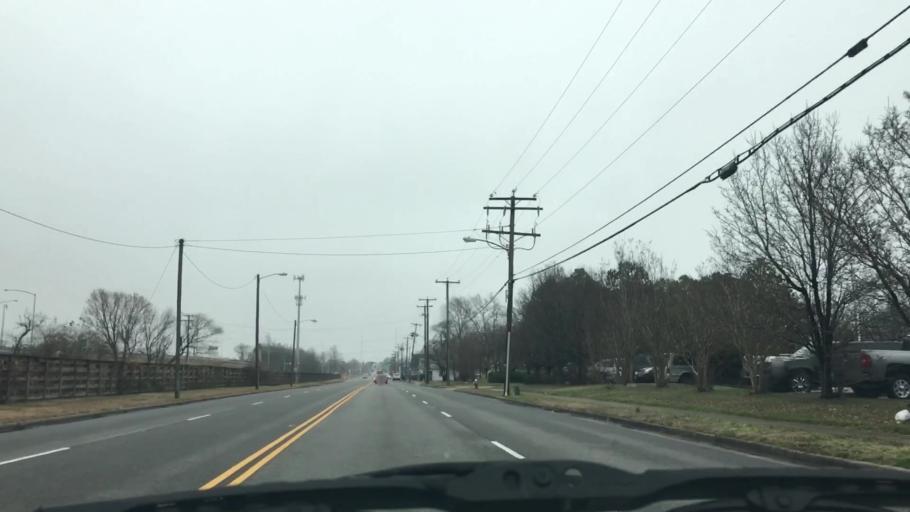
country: US
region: Virginia
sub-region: City of Newport News
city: Newport News
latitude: 36.9937
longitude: -76.4184
